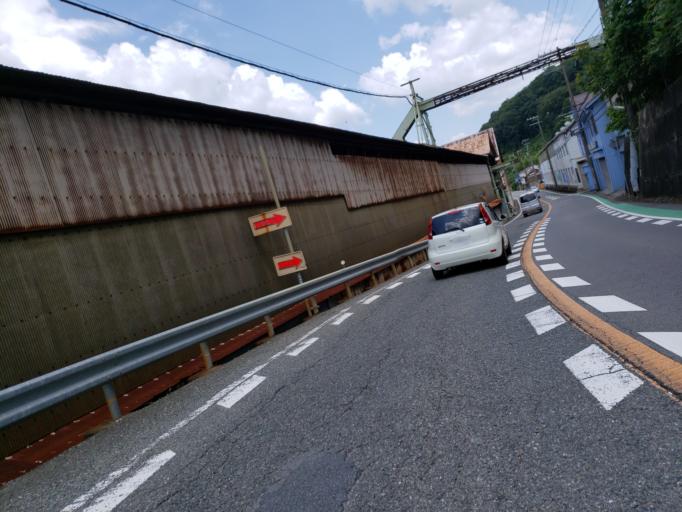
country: JP
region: Hyogo
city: Aioi
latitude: 34.7931
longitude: 134.4683
